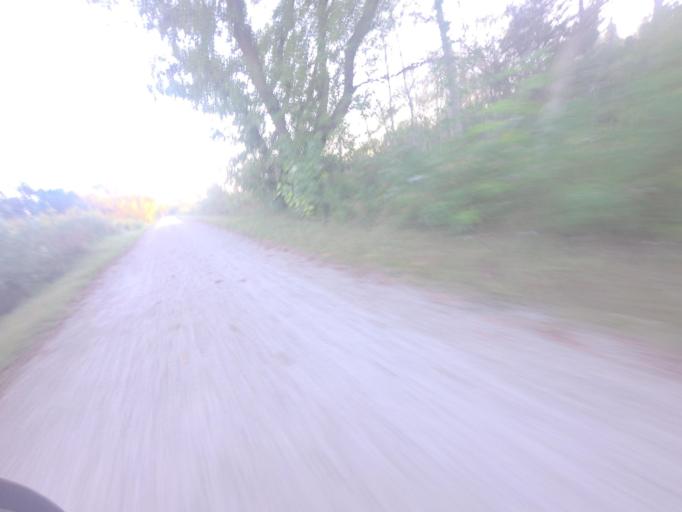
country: CA
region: Ontario
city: Bradford West Gwillimbury
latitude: 43.9719
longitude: -79.8093
